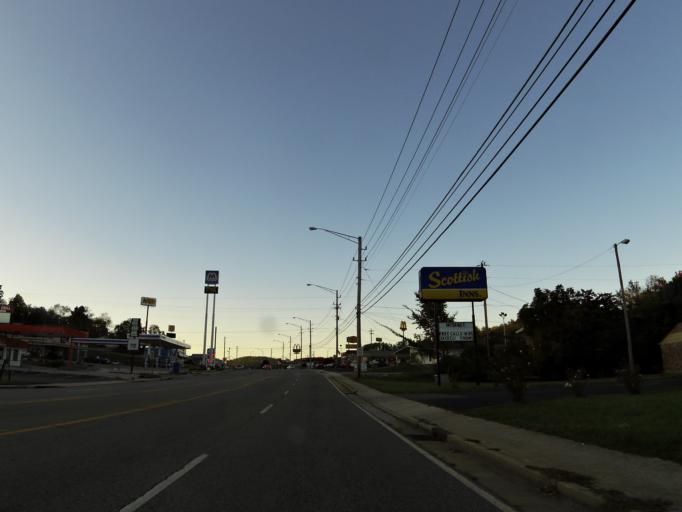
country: US
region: Tennessee
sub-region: Anderson County
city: Rocky Top
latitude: 36.2294
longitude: -84.1580
